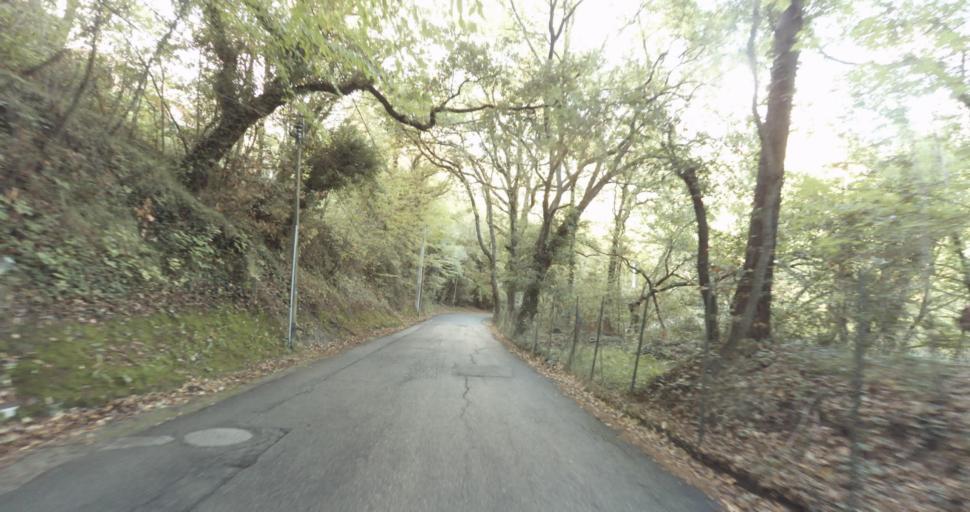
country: FR
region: Provence-Alpes-Cote d'Azur
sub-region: Departement des Alpes-Maritimes
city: Vence
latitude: 43.7337
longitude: 7.1268
